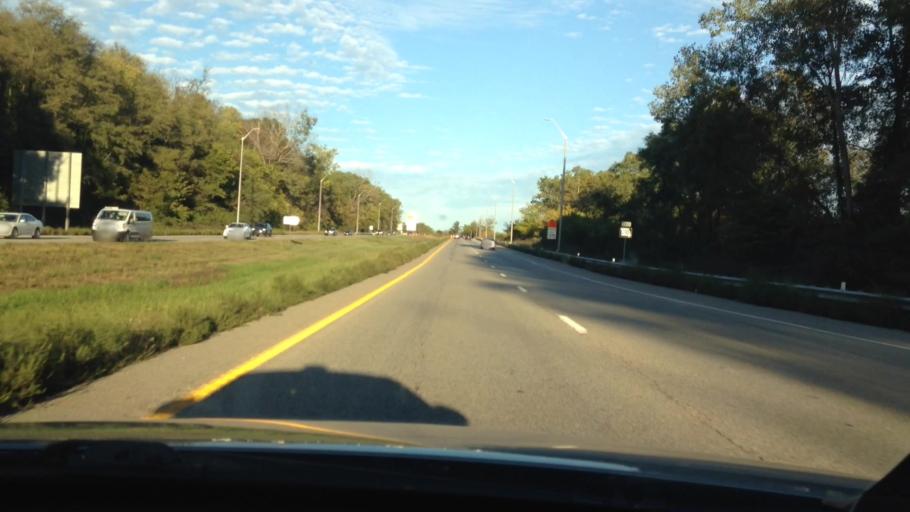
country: US
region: Missouri
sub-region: Clay County
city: Claycomo
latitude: 39.1545
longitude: -94.5110
